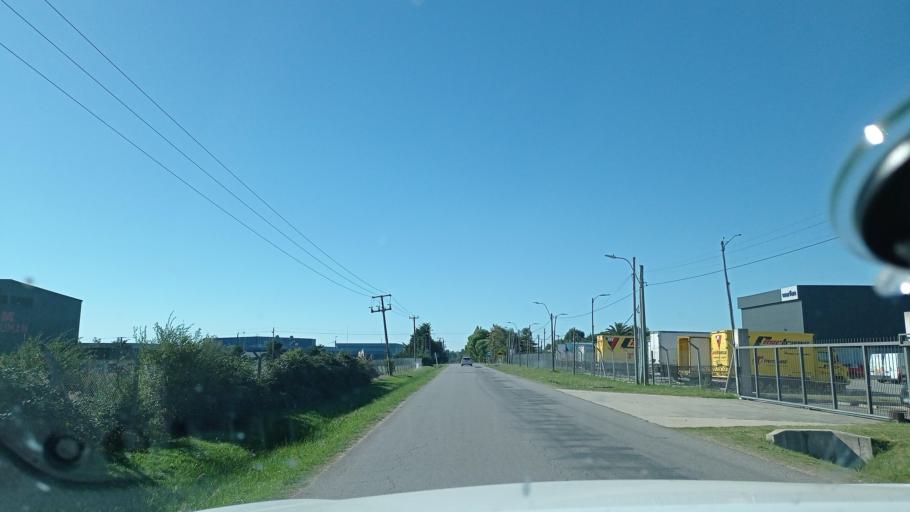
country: UY
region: Canelones
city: Pando
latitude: -34.7595
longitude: -55.9822
